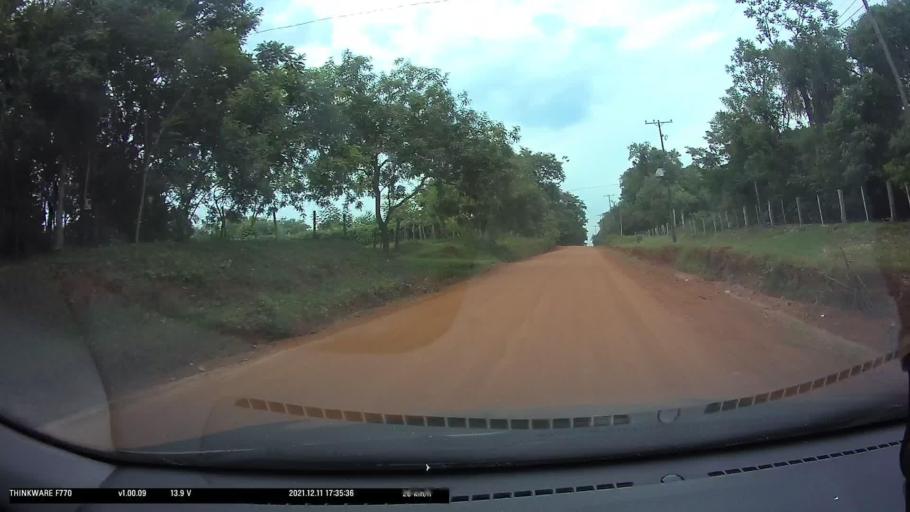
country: PY
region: Cordillera
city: San Bernardino
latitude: -25.3088
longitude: -57.2516
